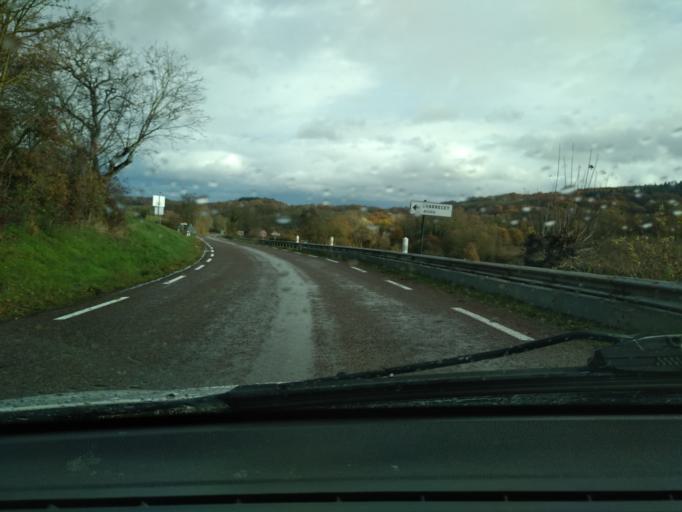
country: FR
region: Bourgogne
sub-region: Departement de Saone-et-Loire
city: Saint-Leger-sur-Dheune
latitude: 46.8365
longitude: 4.6724
